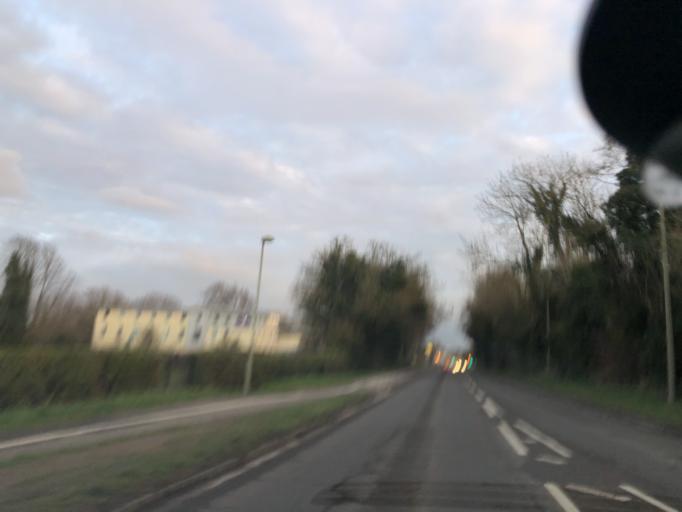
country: GB
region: England
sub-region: Oxfordshire
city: Witney
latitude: 51.7805
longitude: -1.4950
